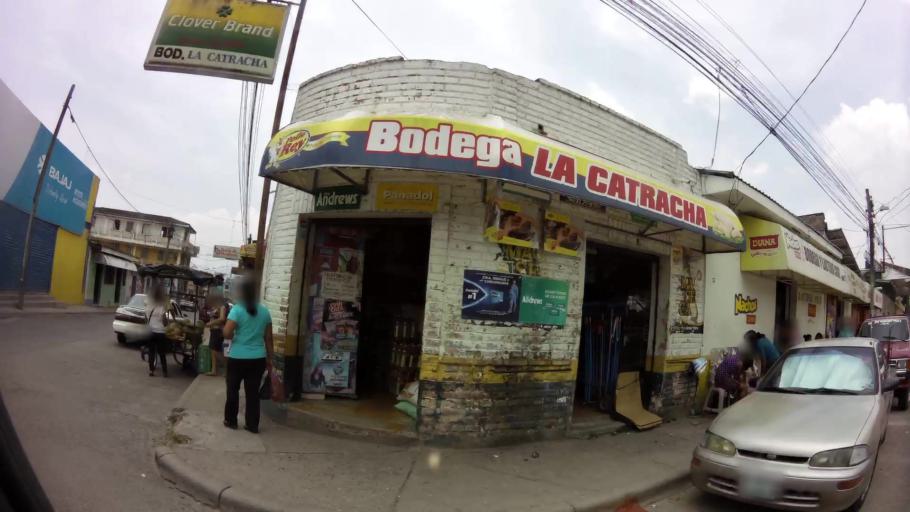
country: HN
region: Comayagua
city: Siguatepeque
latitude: 14.5981
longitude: -87.8306
